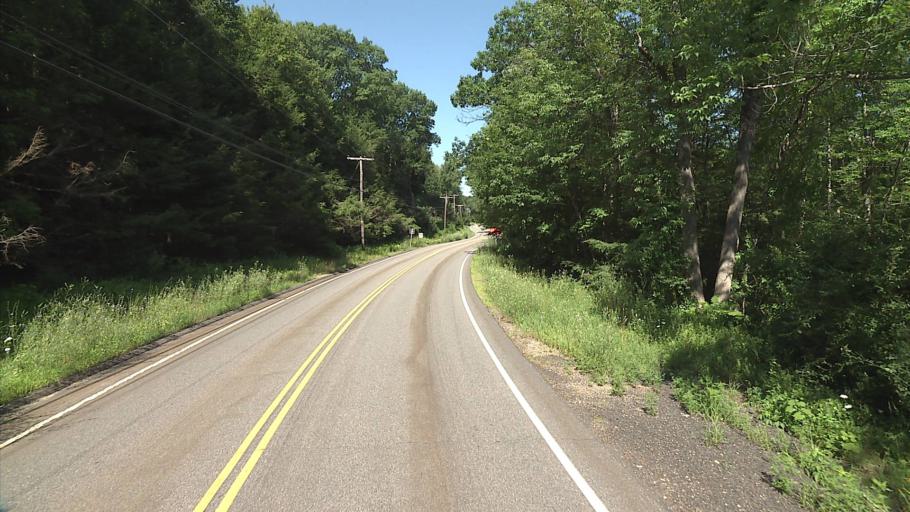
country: US
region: Connecticut
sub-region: Litchfield County
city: Winchester Center
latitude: 41.9156
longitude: -73.1120
